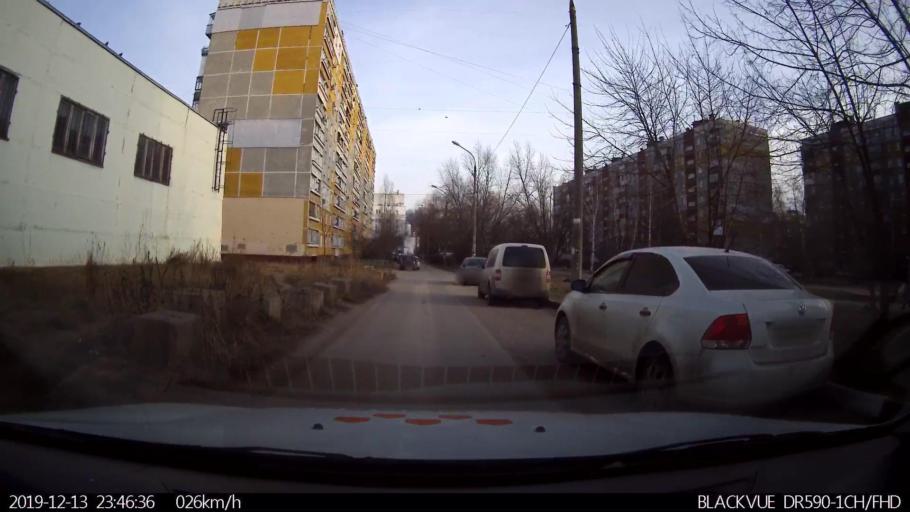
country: RU
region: Nizjnij Novgorod
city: Nizhniy Novgorod
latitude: 56.2932
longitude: 43.9492
